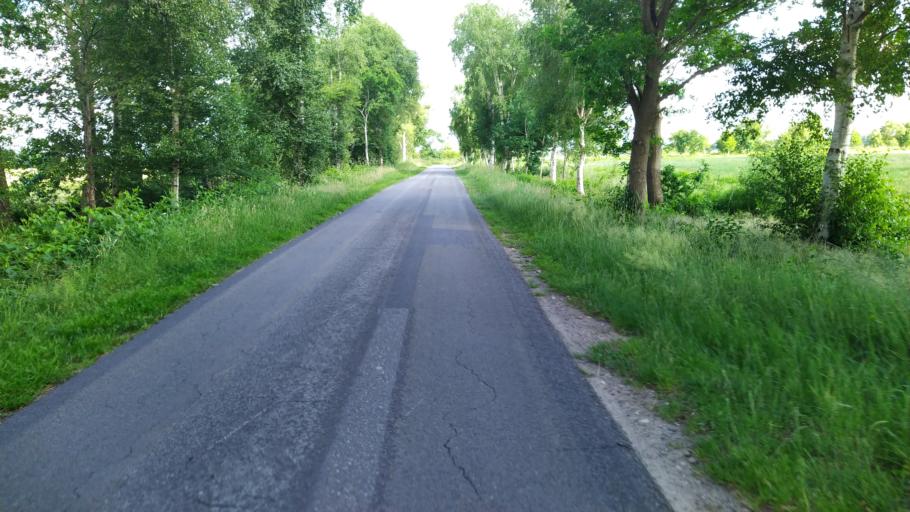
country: DE
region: Lower Saxony
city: Steinau
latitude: 53.6479
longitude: 8.9070
